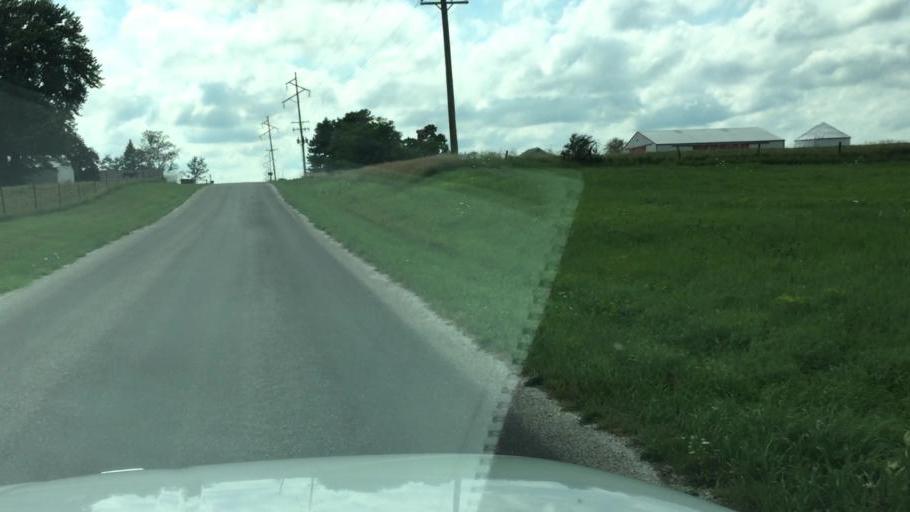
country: US
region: Illinois
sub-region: Hancock County
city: Carthage
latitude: 40.4168
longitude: -91.1620
